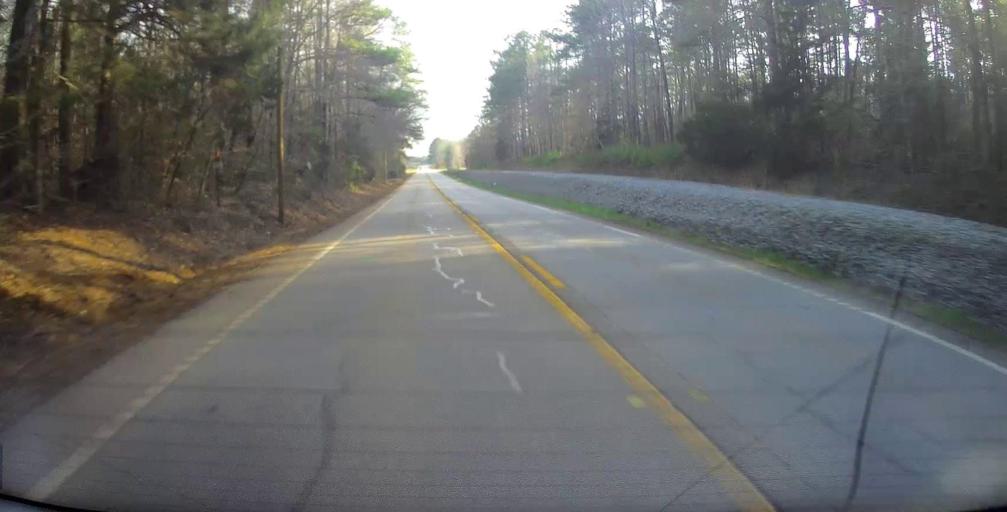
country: US
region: Georgia
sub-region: Harris County
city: Hamilton
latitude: 32.7448
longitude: -84.8699
